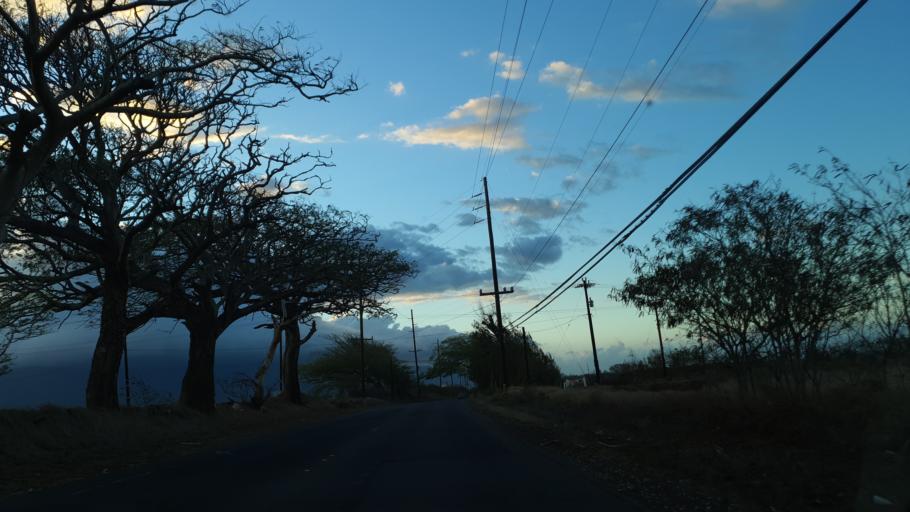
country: US
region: Hawaii
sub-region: Maui County
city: Kahului
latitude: 20.8673
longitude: -156.4340
